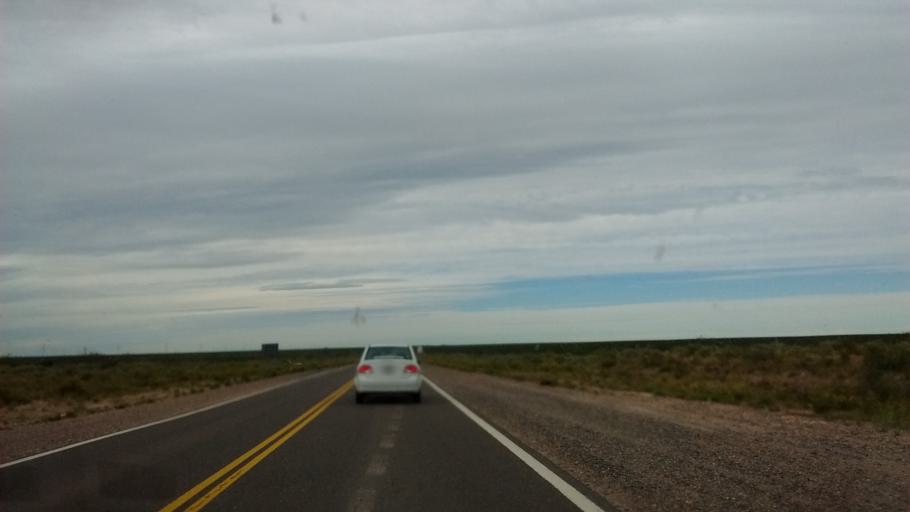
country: AR
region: Rio Negro
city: Contraalmirante Cordero
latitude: -38.3267
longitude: -68.0075
